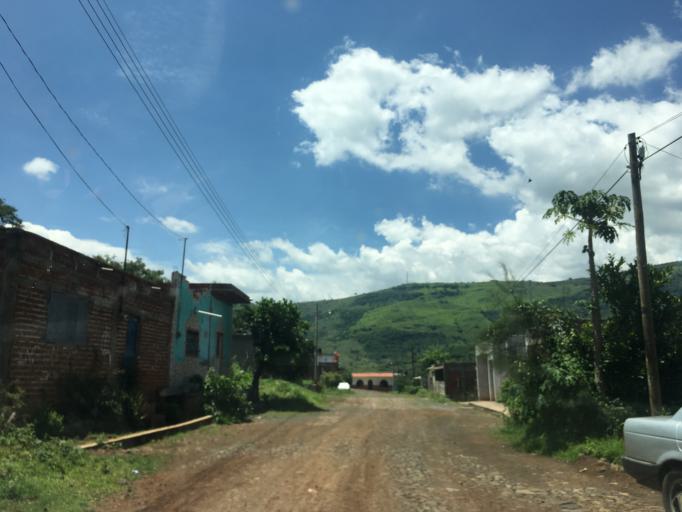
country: MX
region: Nayarit
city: Ixtlan del Rio
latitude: 21.0376
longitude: -104.3513
